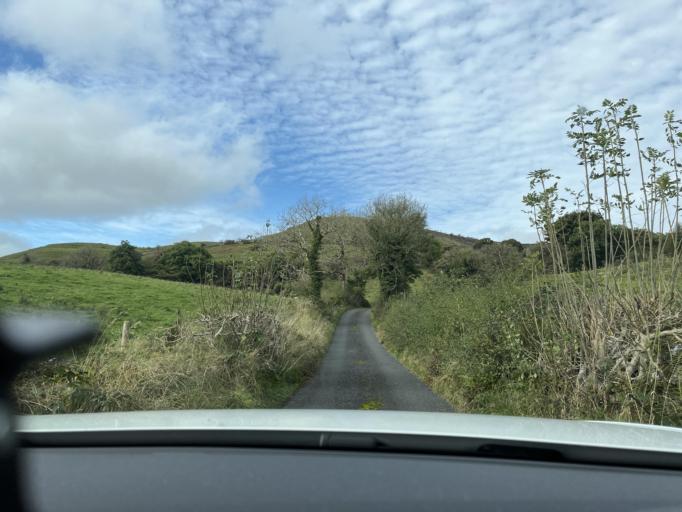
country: IE
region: Connaught
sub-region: Sligo
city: Ballymote
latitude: 54.0476
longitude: -8.4340
